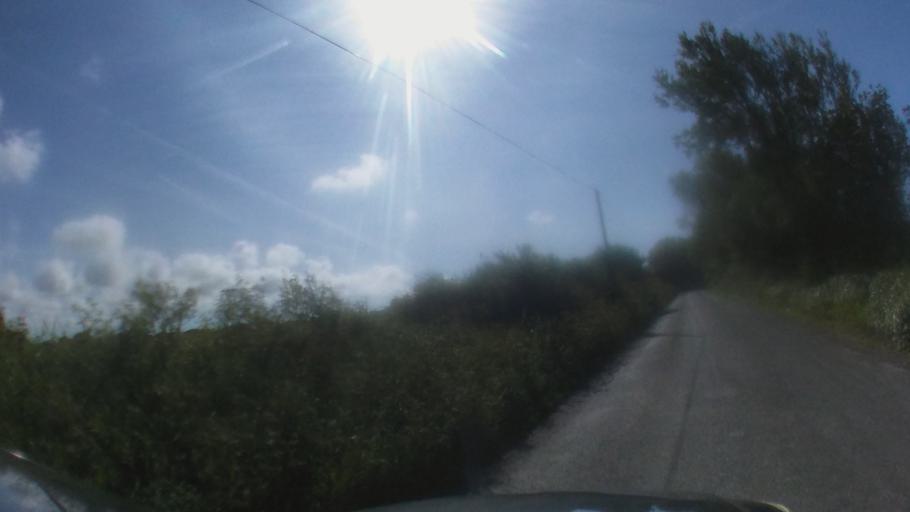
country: IE
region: Leinster
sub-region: Loch Garman
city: Loch Garman
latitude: 52.2256
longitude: -6.5466
